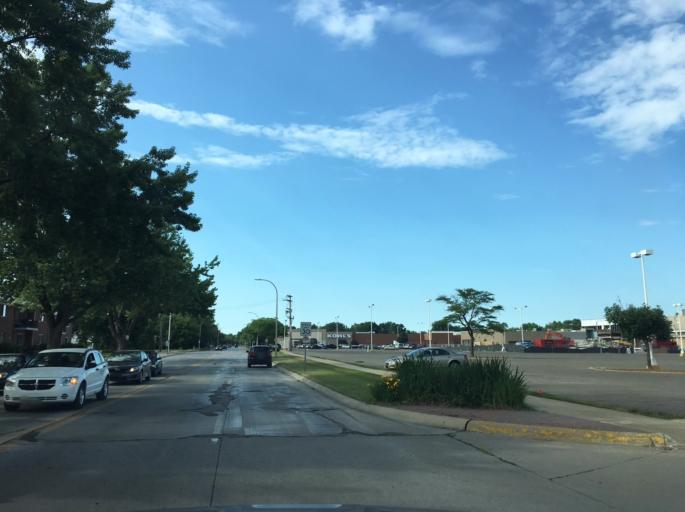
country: US
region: Michigan
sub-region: Macomb County
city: Fraser
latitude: 42.5323
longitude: -82.9192
